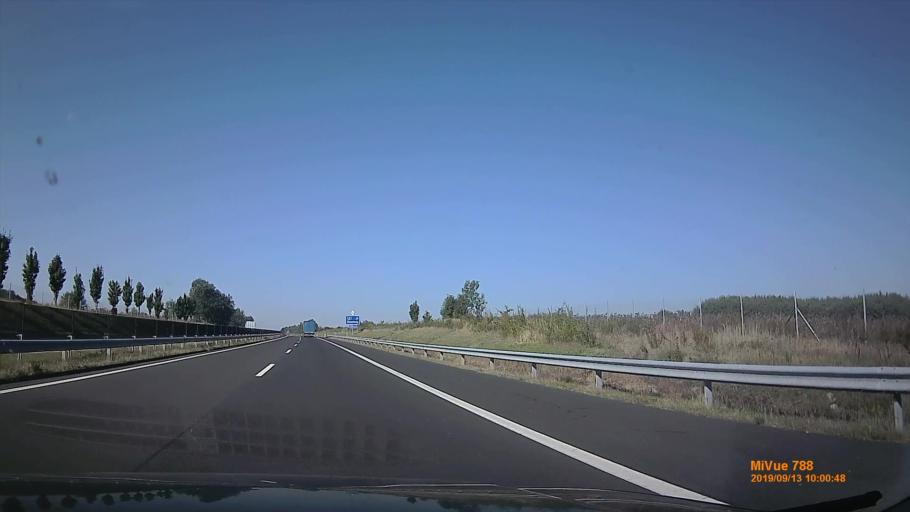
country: HU
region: Zala
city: Becsehely
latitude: 46.4492
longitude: 16.8350
